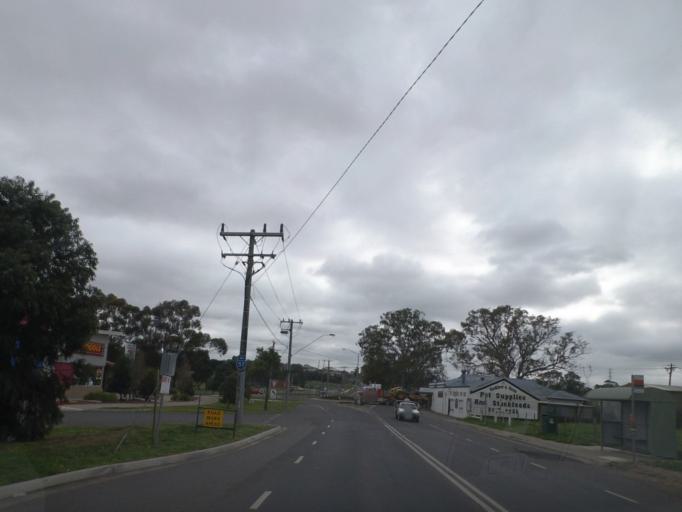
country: AU
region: Victoria
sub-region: Nillumbik
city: Doreen
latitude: -37.6062
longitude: 145.1379
